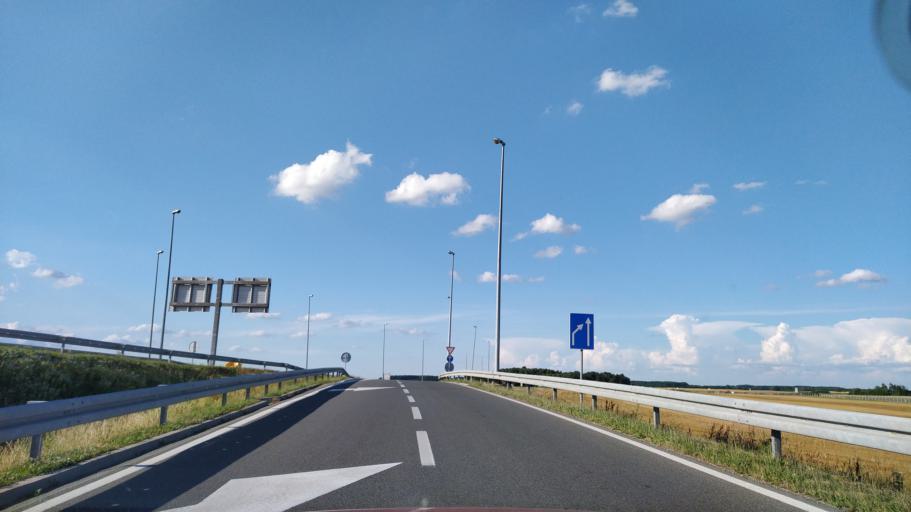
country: HR
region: Virovitick-Podravska
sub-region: Grad Virovitica
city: Virovitica
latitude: 45.8436
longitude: 17.3526
